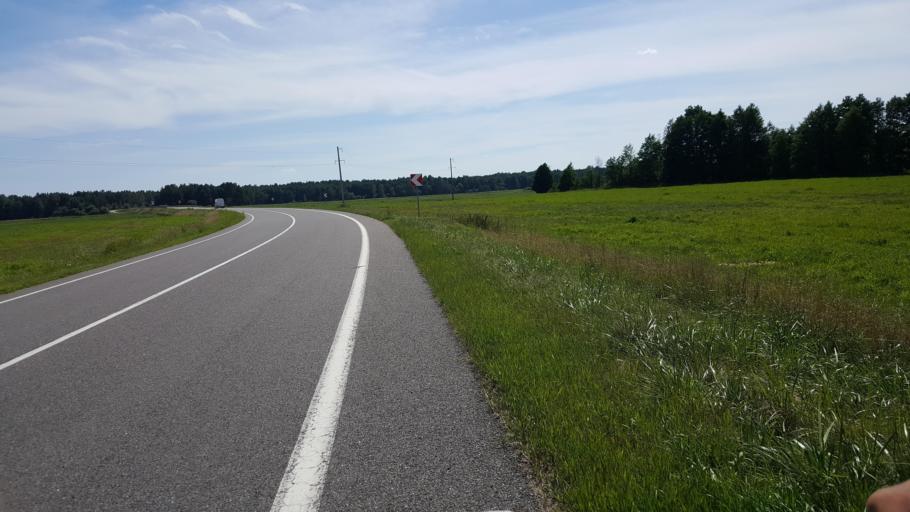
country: BY
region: Brest
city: Pruzhany
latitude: 52.4778
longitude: 24.1557
